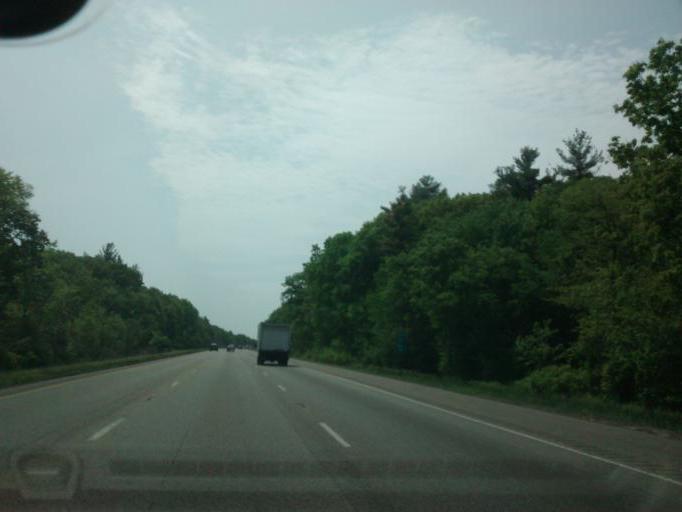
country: US
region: Massachusetts
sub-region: Middlesex County
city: Hopkinton
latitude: 42.2403
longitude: -71.5542
